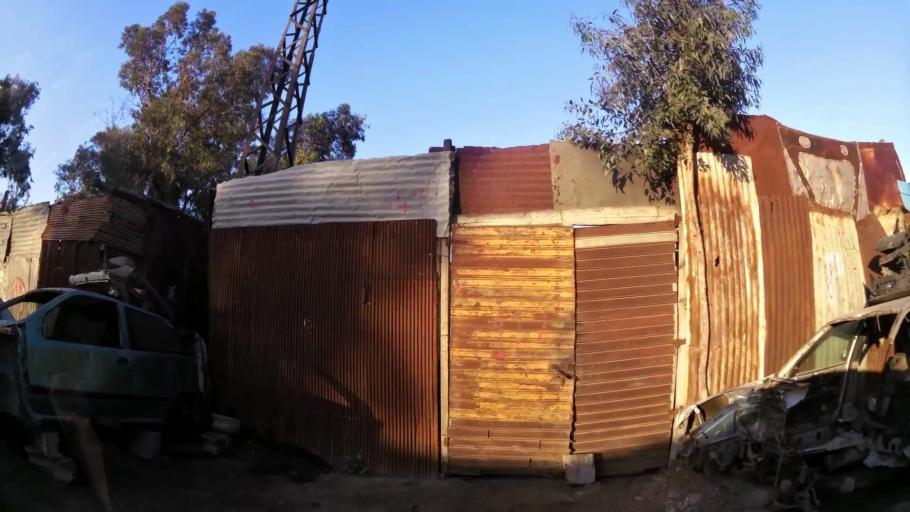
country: MA
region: Oriental
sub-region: Oujda-Angad
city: Oujda
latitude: 34.7115
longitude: -1.9111
